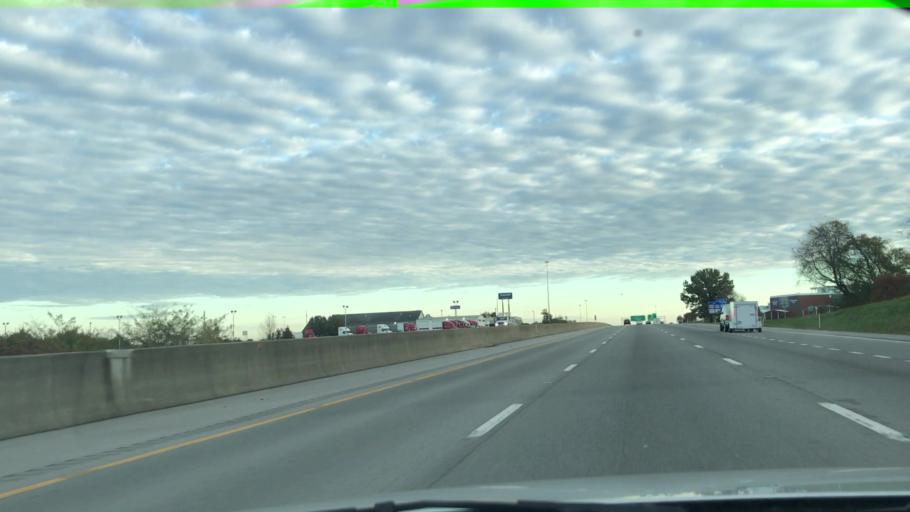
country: US
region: Kentucky
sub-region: Simpson County
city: Franklin
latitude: 36.7085
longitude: -86.5259
